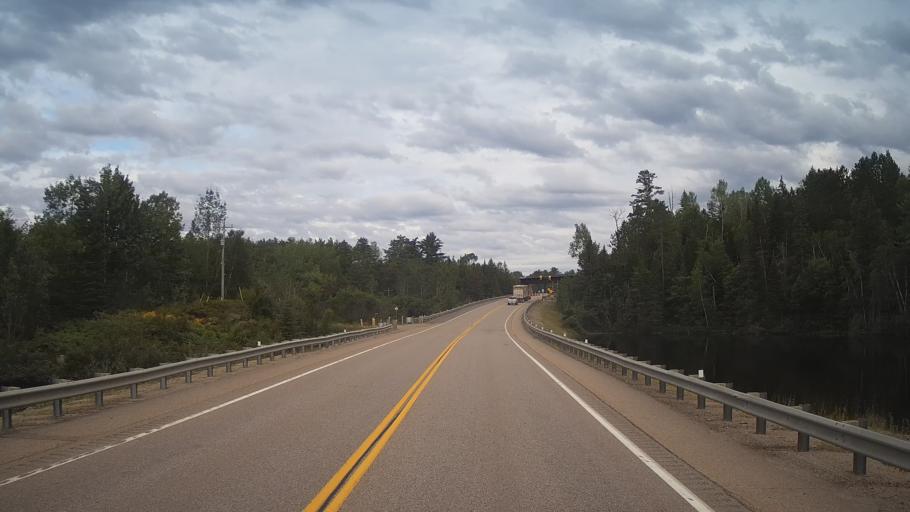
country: CA
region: Ontario
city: Deep River
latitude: 46.2267
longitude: -78.0711
